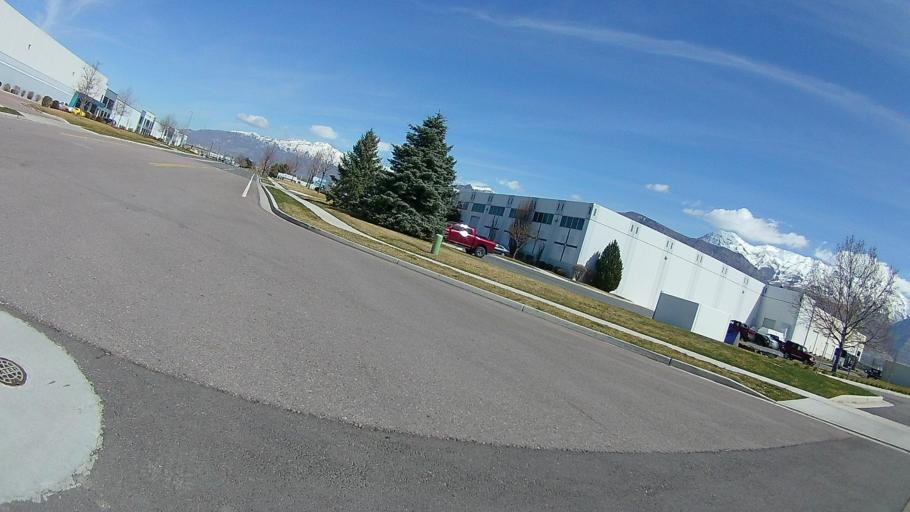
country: US
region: Utah
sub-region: Utah County
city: American Fork
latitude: 40.3501
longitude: -111.7811
